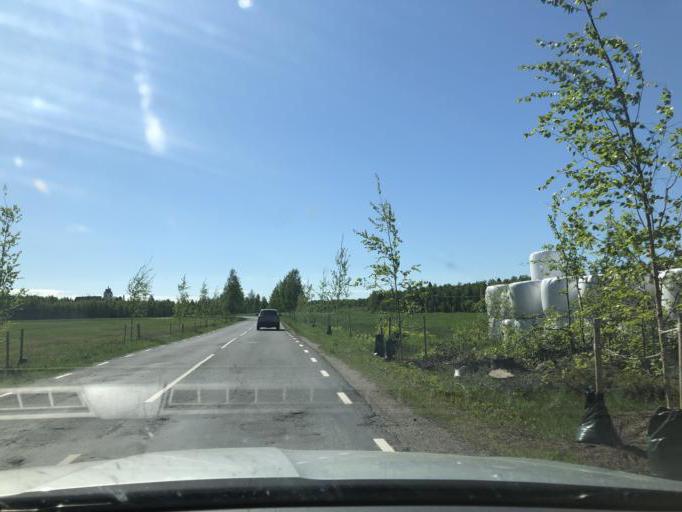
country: SE
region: Norrbotten
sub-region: Lulea Kommun
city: Gammelstad
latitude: 65.6533
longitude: 22.0166
